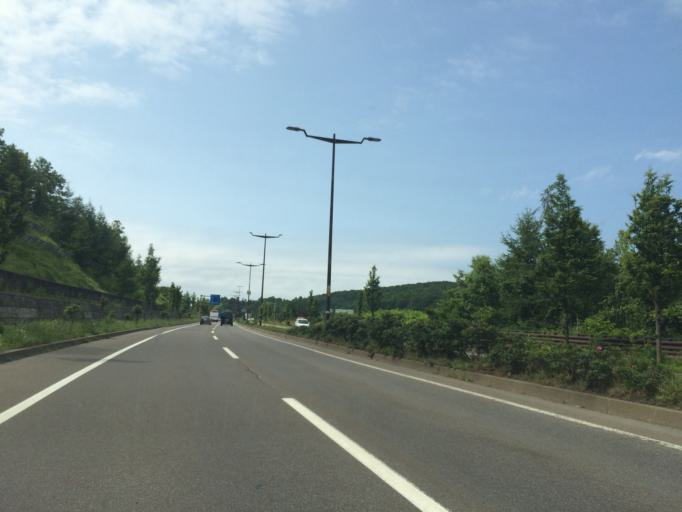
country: JP
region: Hokkaido
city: Otaru
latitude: 43.2147
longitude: 140.9577
